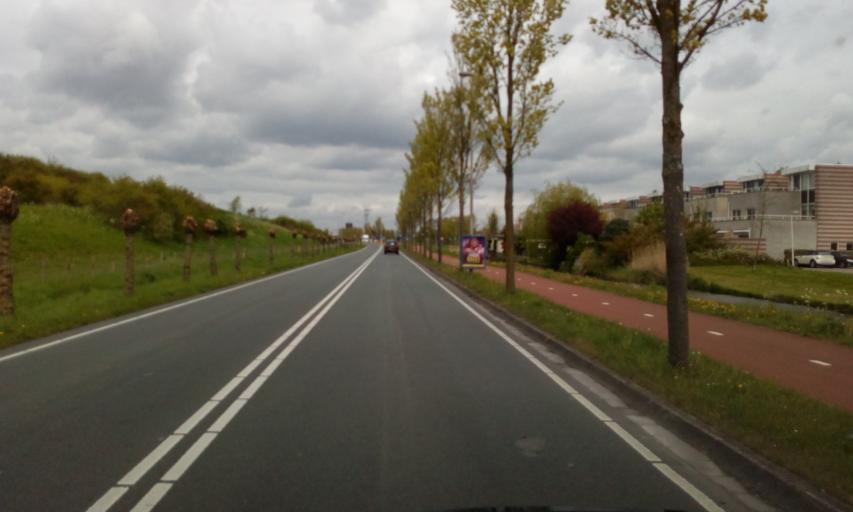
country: NL
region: South Holland
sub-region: Gemeente Barendrecht
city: Barendrecht
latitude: 51.8518
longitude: 4.5179
